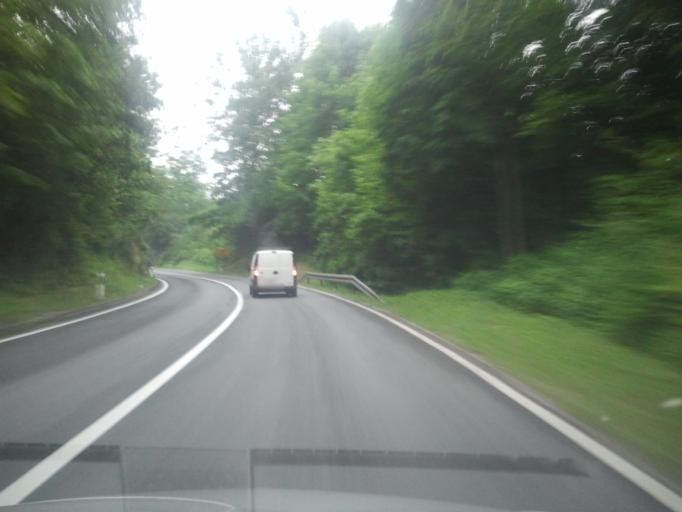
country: HR
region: Karlovacka
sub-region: Grad Karlovac
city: Slunj
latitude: 45.1949
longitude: 15.5554
